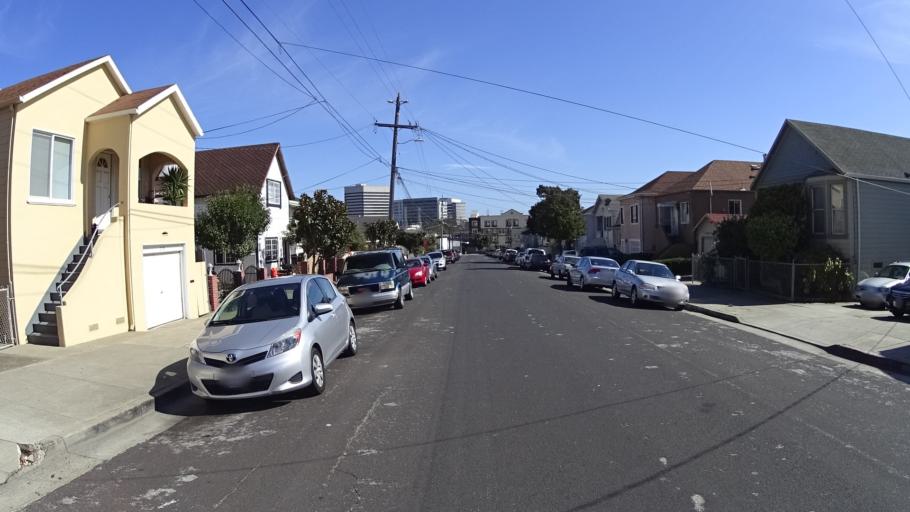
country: US
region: California
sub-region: San Mateo County
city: South San Francisco
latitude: 37.6599
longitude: -122.4080
